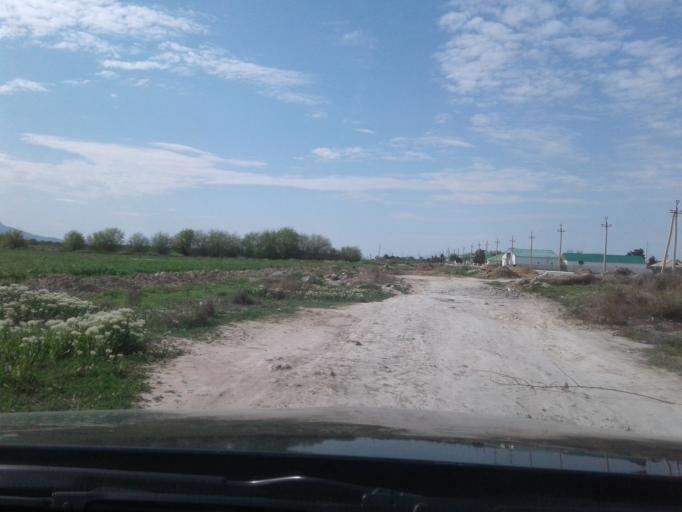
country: TM
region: Ahal
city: Ashgabat
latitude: 37.9801
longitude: 58.2899
